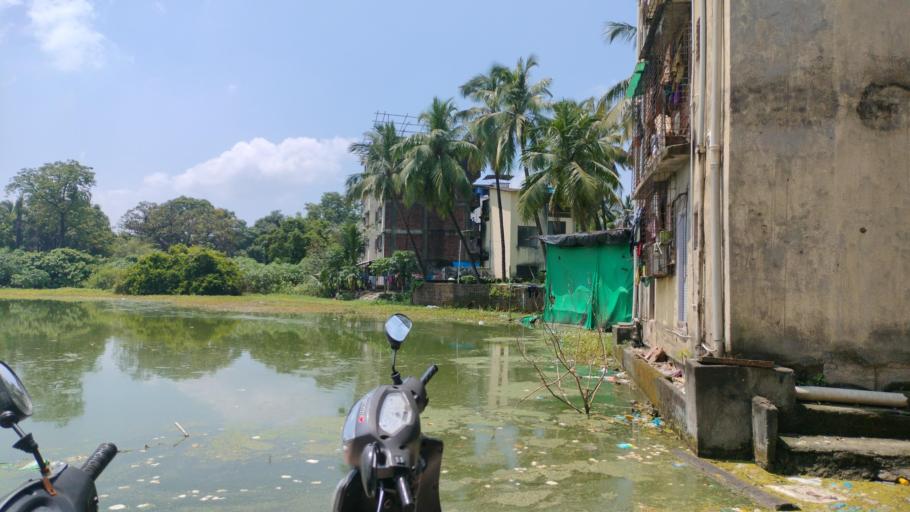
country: IN
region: Maharashtra
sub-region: Thane
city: Virar
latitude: 19.4122
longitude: 72.8006
